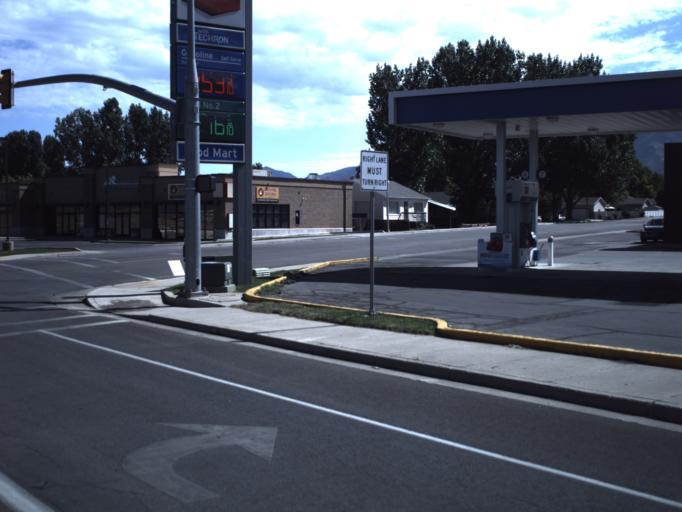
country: US
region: Utah
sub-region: Utah County
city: Salem
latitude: 40.0604
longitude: -111.6688
